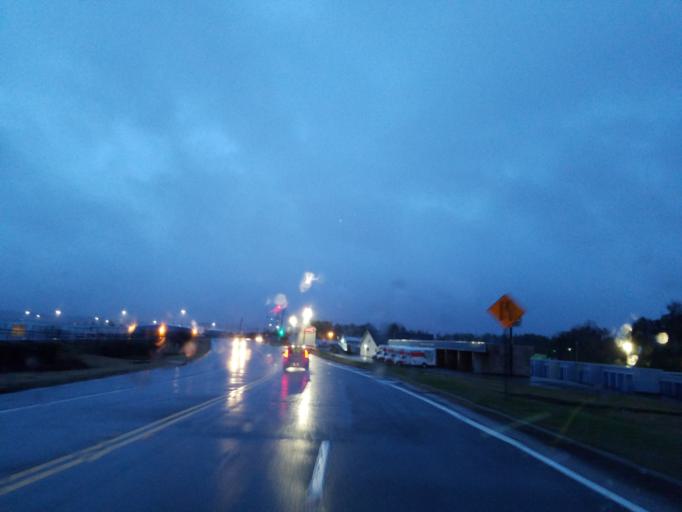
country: US
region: Georgia
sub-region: Cobb County
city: Kennesaw
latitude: 34.0128
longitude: -84.6083
